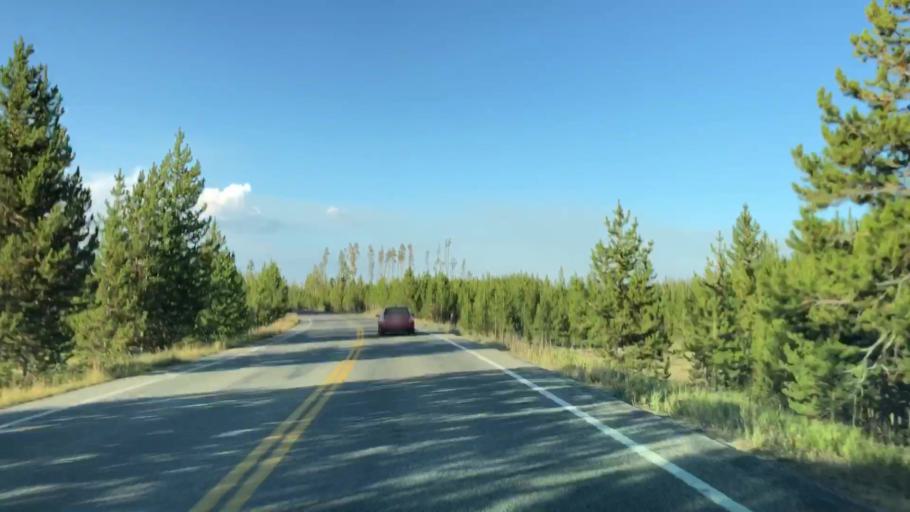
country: US
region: Montana
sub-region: Gallatin County
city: West Yellowstone
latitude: 44.6539
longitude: -110.9924
